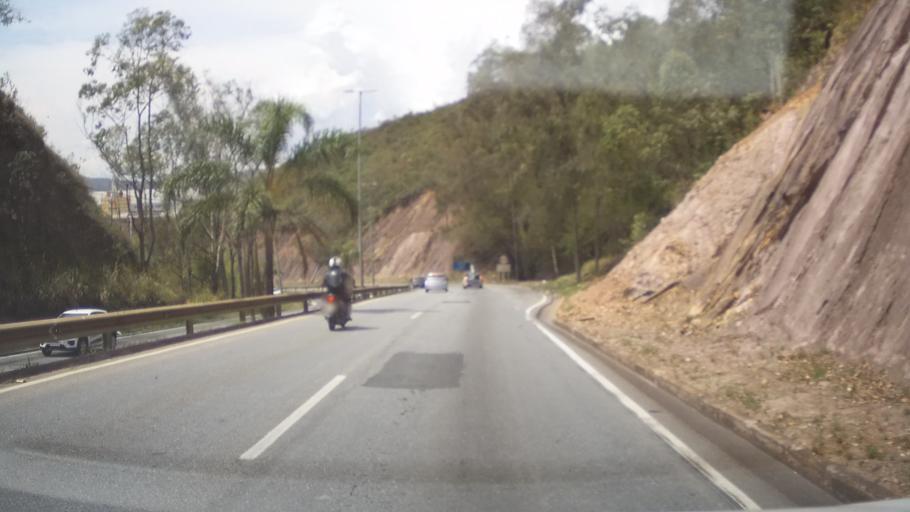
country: BR
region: Minas Gerais
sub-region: Belo Horizonte
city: Belo Horizonte
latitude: -19.9883
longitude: -43.9317
